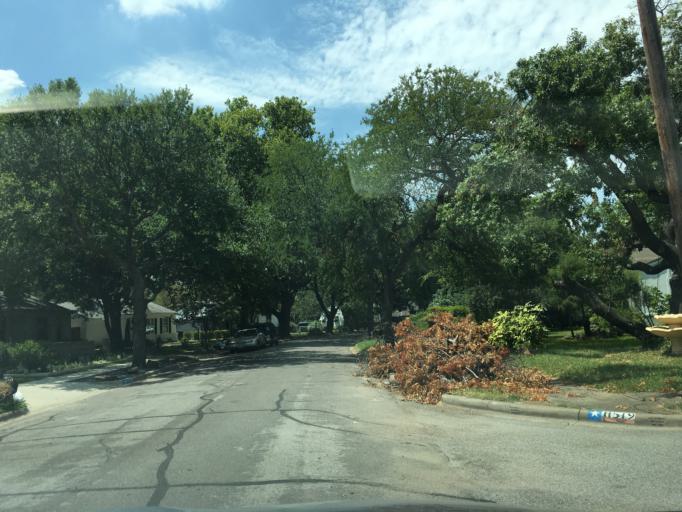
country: US
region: Texas
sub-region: Dallas County
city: Garland
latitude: 32.8572
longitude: -96.6806
